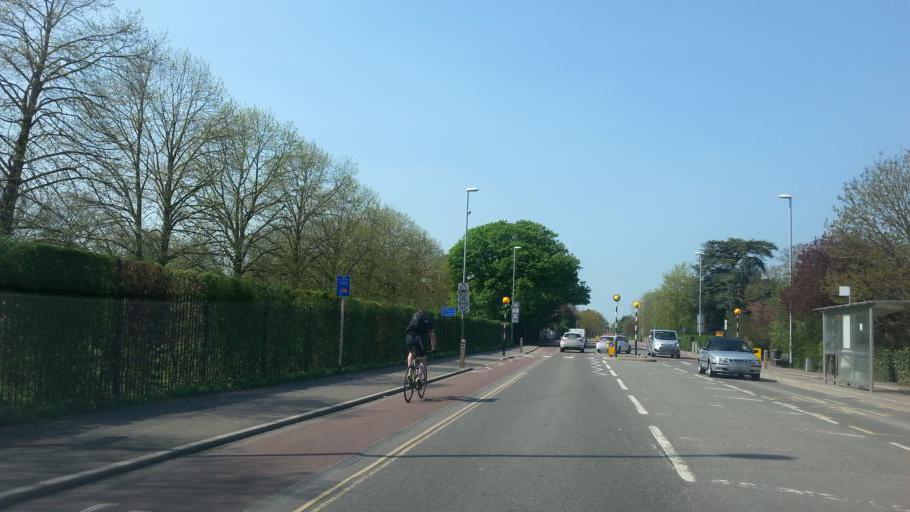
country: GB
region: England
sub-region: Cambridgeshire
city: Cambridge
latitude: 52.2172
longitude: 0.1044
